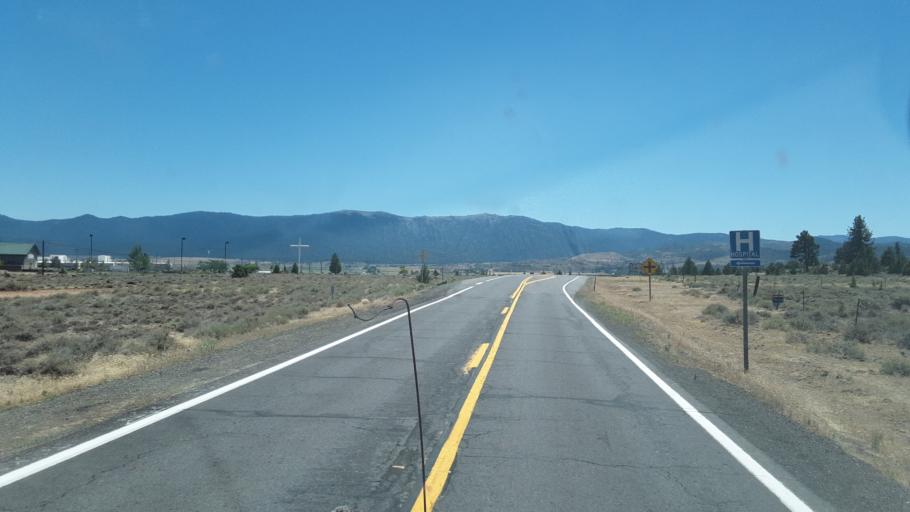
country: US
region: California
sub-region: Lassen County
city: Susanville
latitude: 40.4408
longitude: -120.6289
